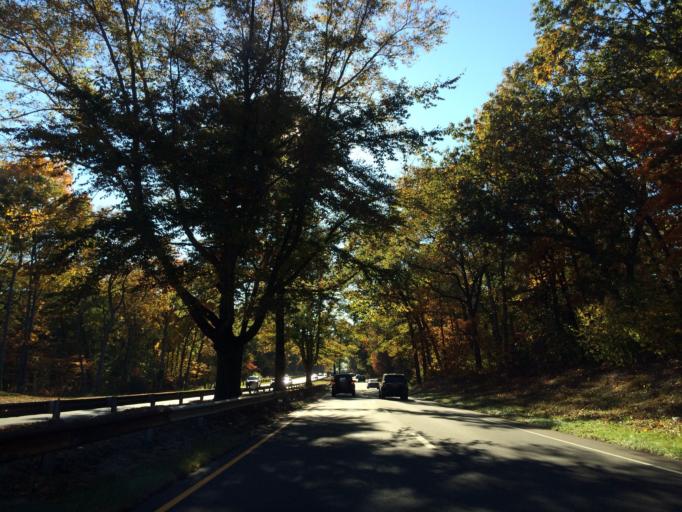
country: US
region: Connecticut
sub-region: Fairfield County
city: Norwalk
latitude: 41.1521
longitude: -73.4059
